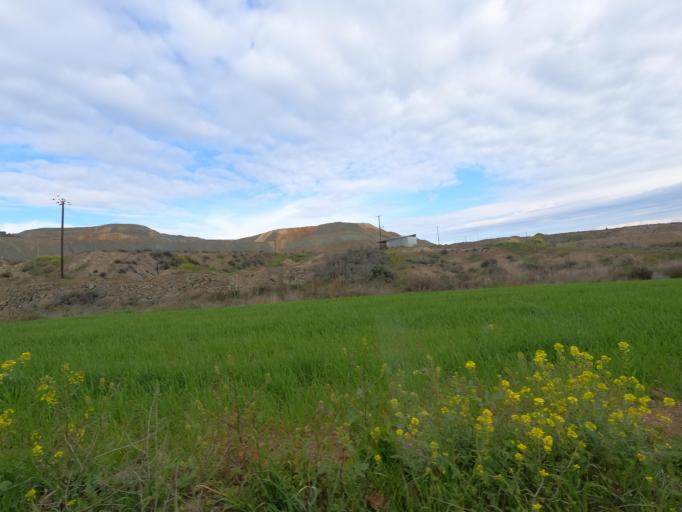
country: CY
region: Lefkosia
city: Lefka
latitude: 35.0924
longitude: 32.9084
